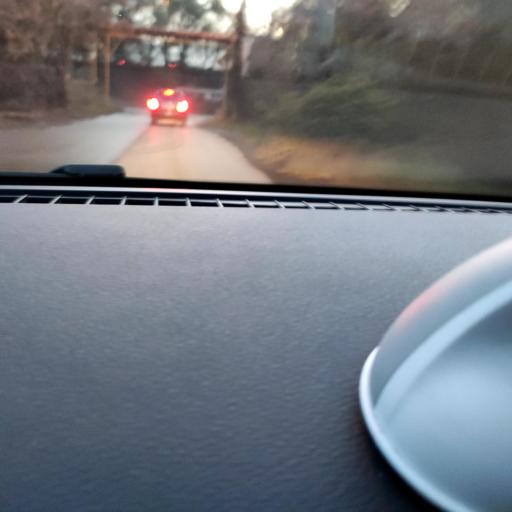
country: RU
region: Samara
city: Samara
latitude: 53.2009
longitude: 50.2448
